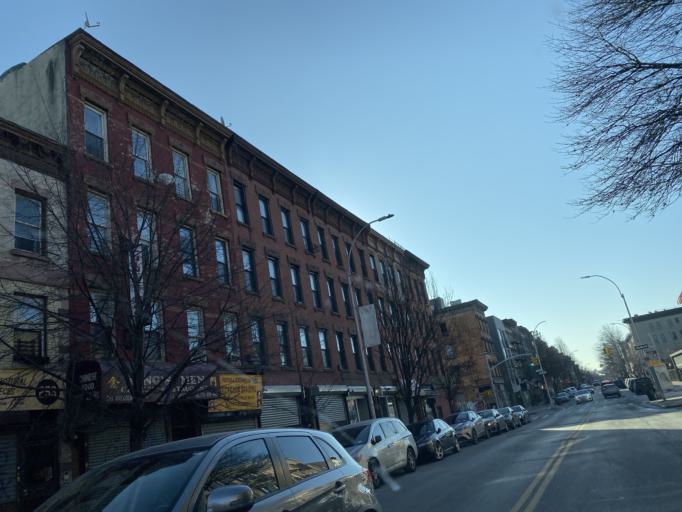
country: US
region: New York
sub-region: Kings County
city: Brooklyn
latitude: 40.6840
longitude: -73.9293
